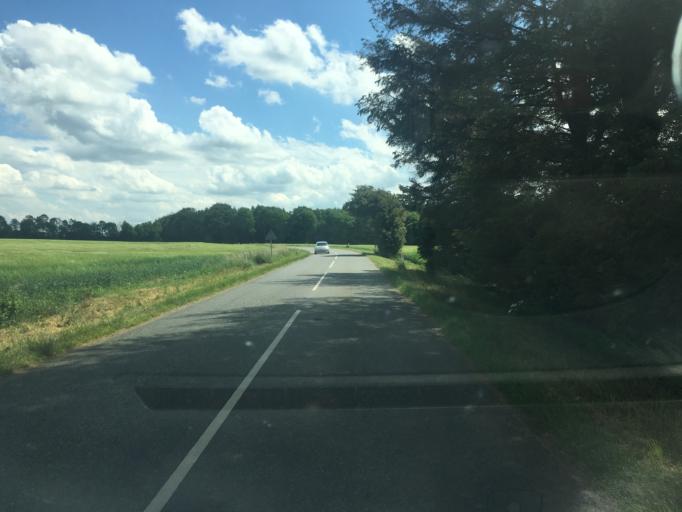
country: DK
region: South Denmark
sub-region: Haderslev Kommune
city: Vojens
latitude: 55.2810
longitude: 9.3187
